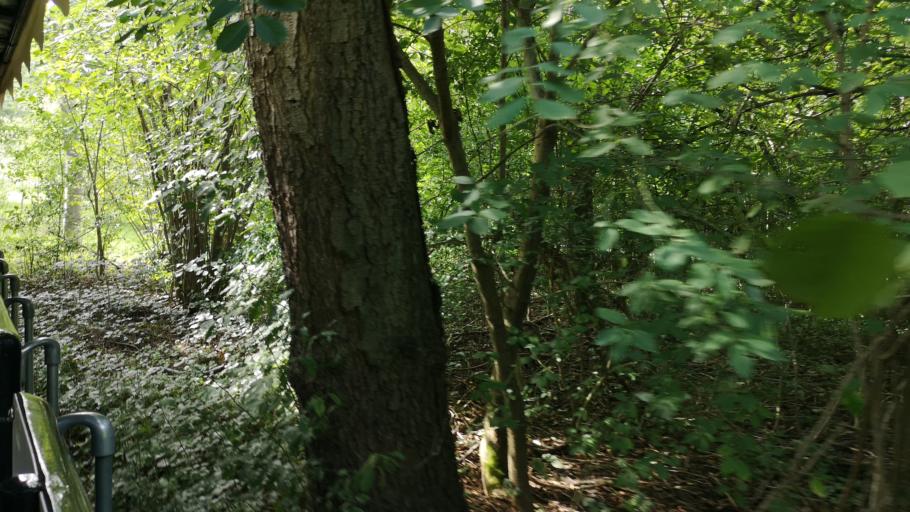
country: NL
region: North Holland
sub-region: Gemeente Ouder-Amstel
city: Ouderkerk aan de Amstel
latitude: 52.3280
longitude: 4.8929
